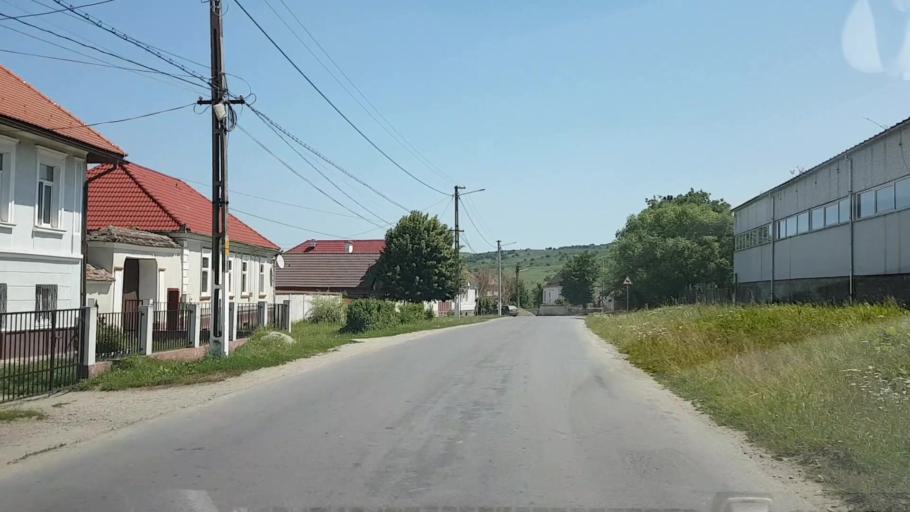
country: RO
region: Brasov
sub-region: Comuna Cincu
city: Cincu
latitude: 45.9168
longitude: 24.8032
